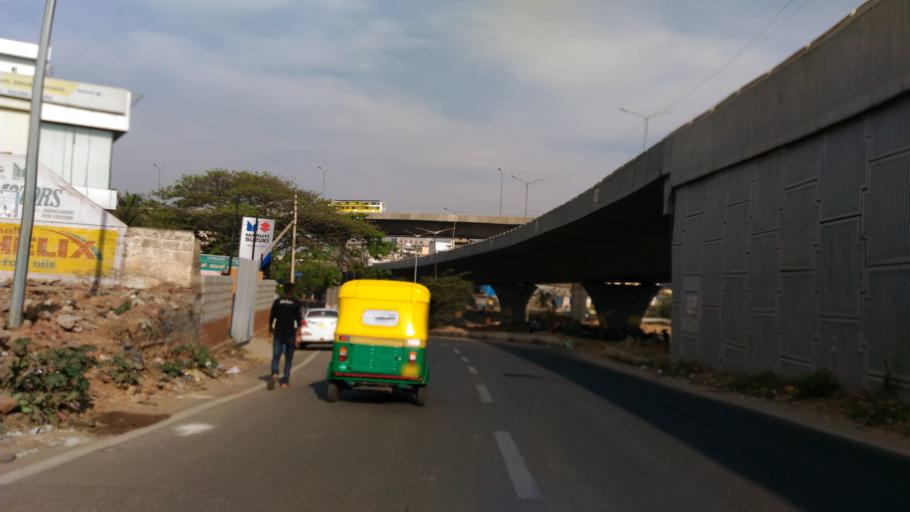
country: IN
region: Karnataka
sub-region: Bangalore Urban
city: Bangalore
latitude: 12.9446
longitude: 77.5294
